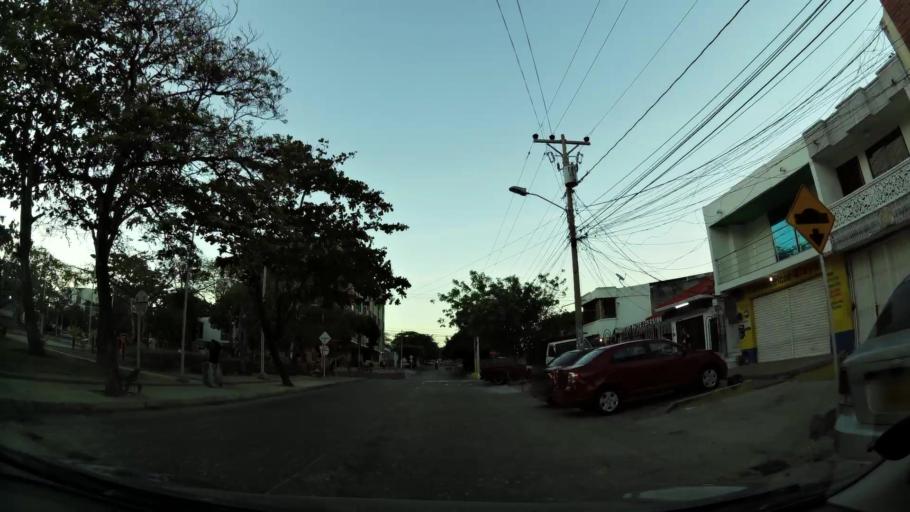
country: CO
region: Atlantico
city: Barranquilla
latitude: 10.9801
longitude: -74.8090
